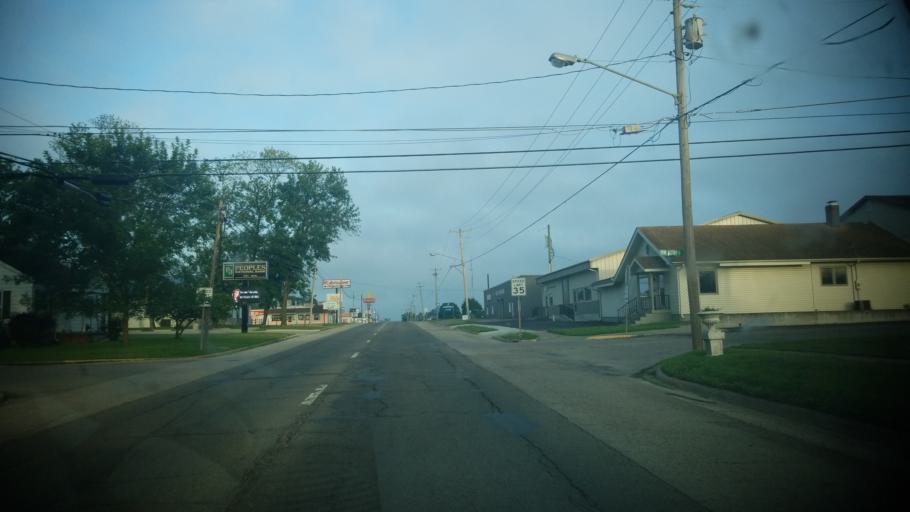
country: US
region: Illinois
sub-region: Wayne County
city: Fairfield
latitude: 38.3797
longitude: -88.3729
